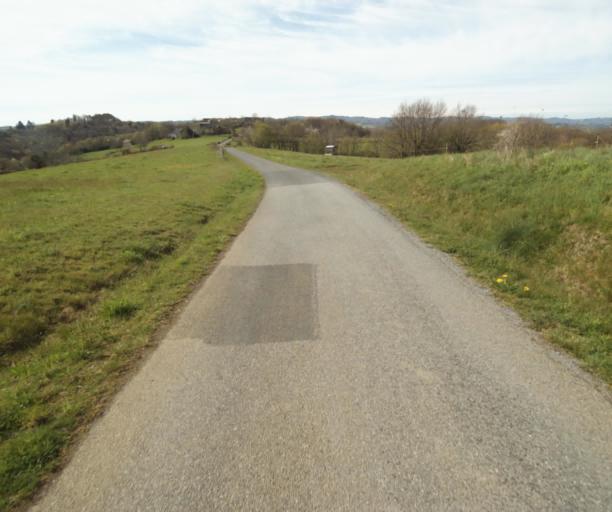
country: FR
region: Limousin
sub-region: Departement de la Correze
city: Laguenne
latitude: 45.2662
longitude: 1.8076
